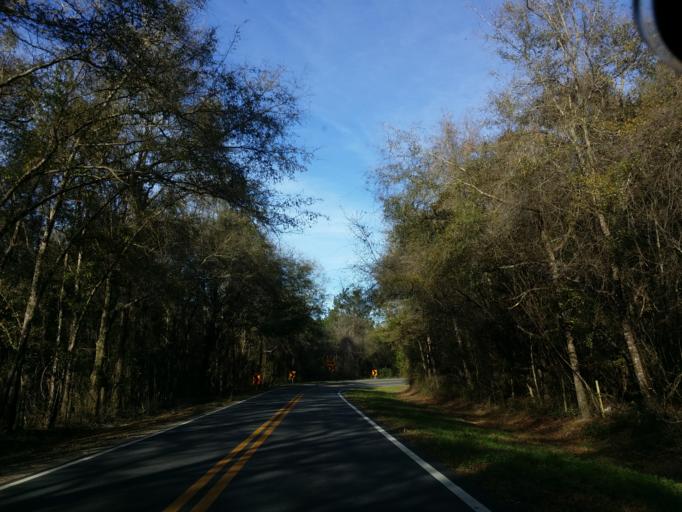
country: US
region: Florida
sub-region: Leon County
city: Woodville
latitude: 30.3794
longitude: -84.1543
